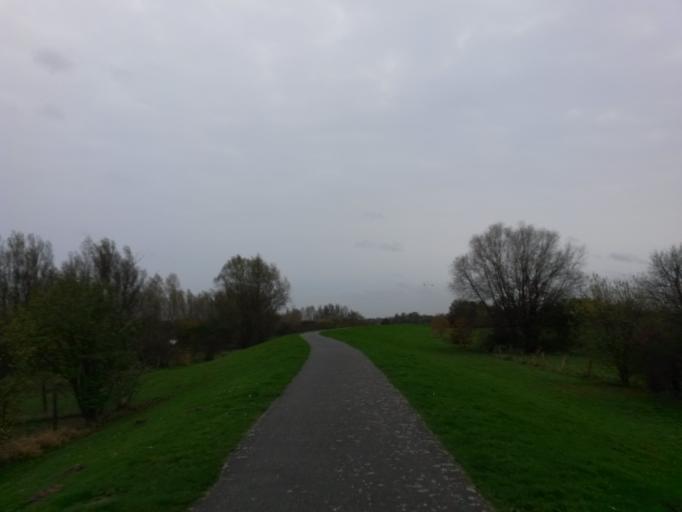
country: DE
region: Bremen
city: Bremen
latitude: 53.0523
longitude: 8.8718
